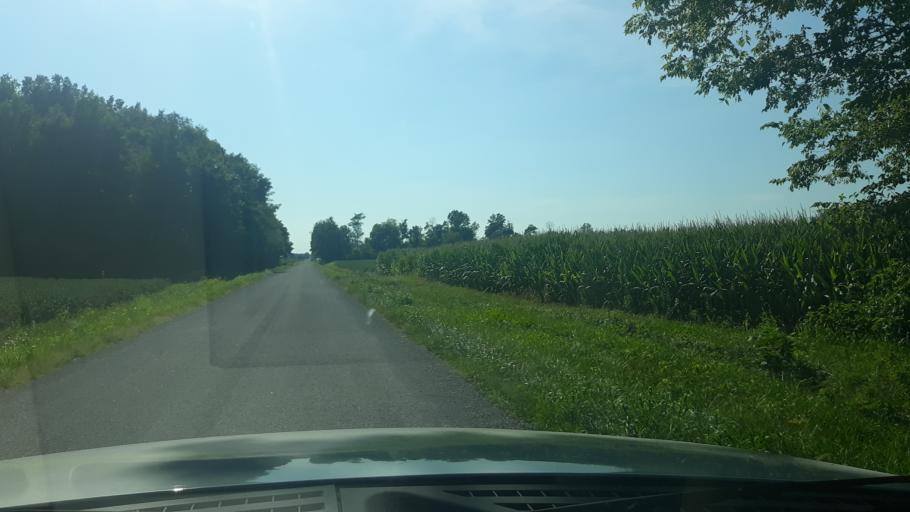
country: US
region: Illinois
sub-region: Saline County
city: Eldorado
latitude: 37.8632
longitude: -88.4886
